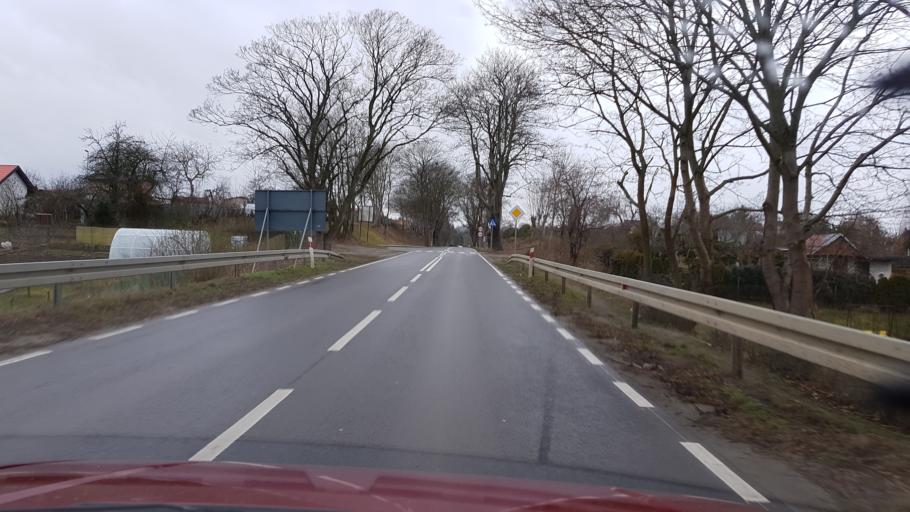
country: PL
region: West Pomeranian Voivodeship
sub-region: Powiat gryfinski
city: Gryfino
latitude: 53.2581
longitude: 14.5043
